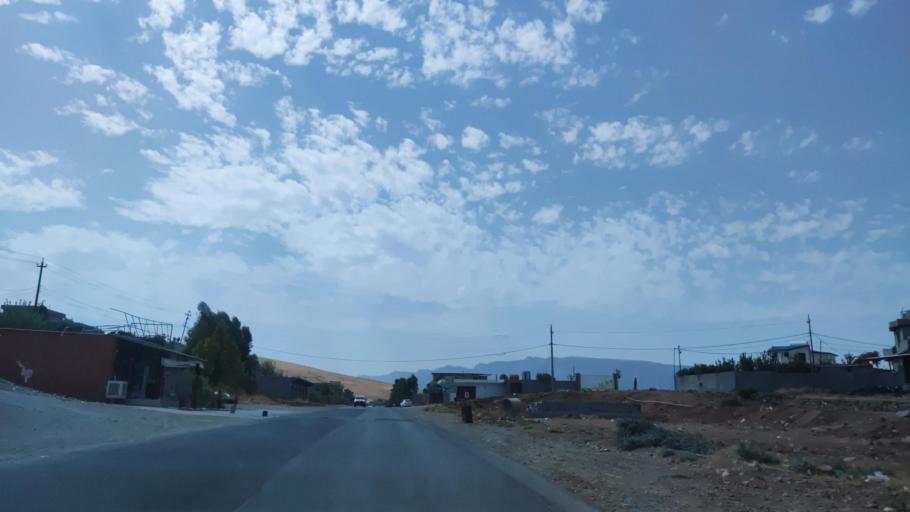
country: IQ
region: Arbil
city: Shaqlawah
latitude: 36.4785
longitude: 44.3977
